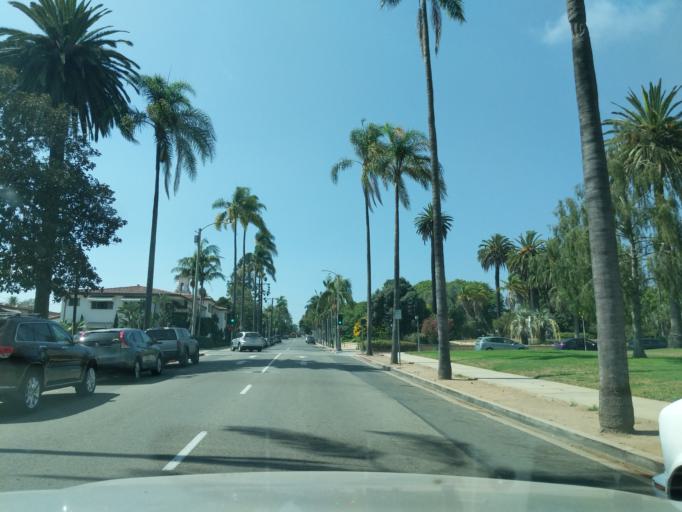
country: US
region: California
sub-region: Santa Barbara County
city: Santa Barbara
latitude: 34.4280
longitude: -119.7055
